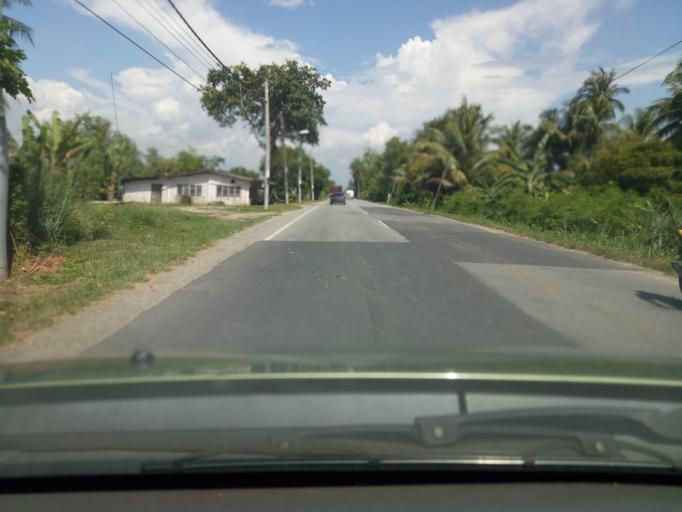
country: MY
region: Kedah
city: Alor Setar
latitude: 5.9734
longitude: 100.4079
